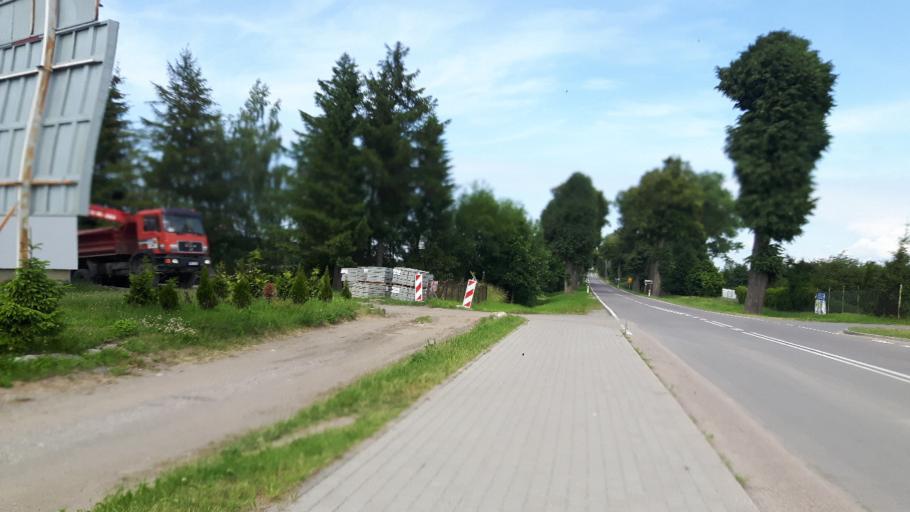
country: PL
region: Warmian-Masurian Voivodeship
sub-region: Powiat braniewski
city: Braniewo
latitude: 54.4040
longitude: 19.8564
